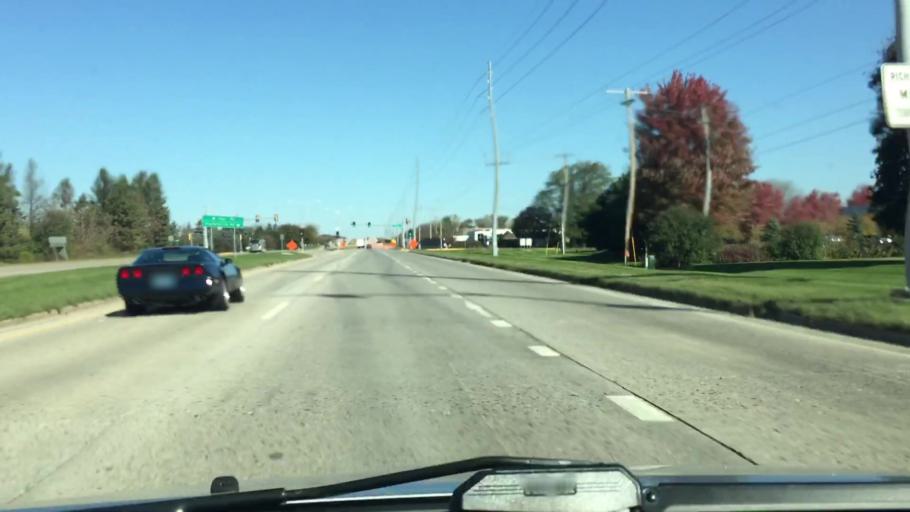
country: US
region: Wisconsin
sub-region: Waukesha County
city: Pewaukee
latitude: 43.0639
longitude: -88.2056
